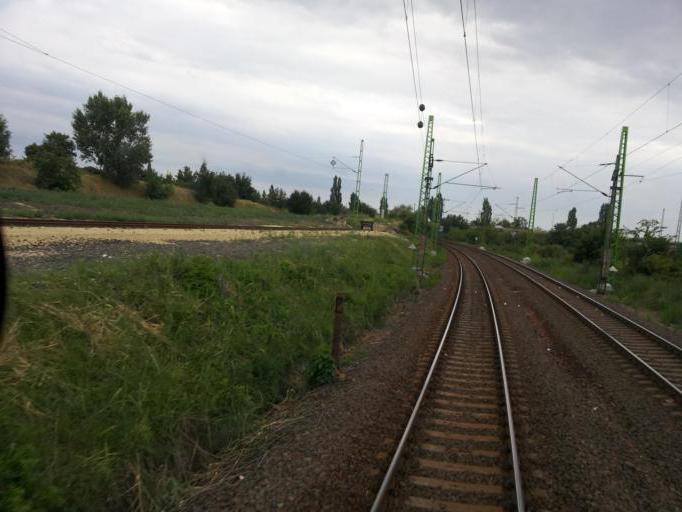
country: HU
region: Fejer
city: Szekesfehervar
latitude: 47.1783
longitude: 18.4110
